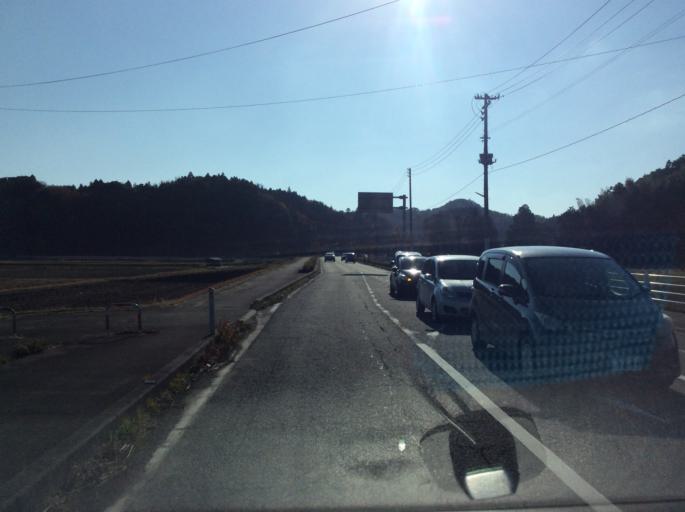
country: JP
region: Fukushima
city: Iwaki
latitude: 37.0315
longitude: 140.9353
